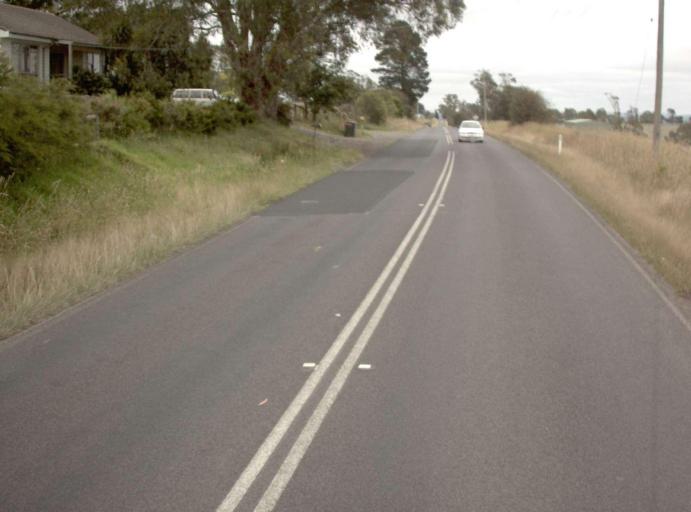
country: AU
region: Victoria
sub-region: Cardinia
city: Bunyip
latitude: -38.1111
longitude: 145.8186
